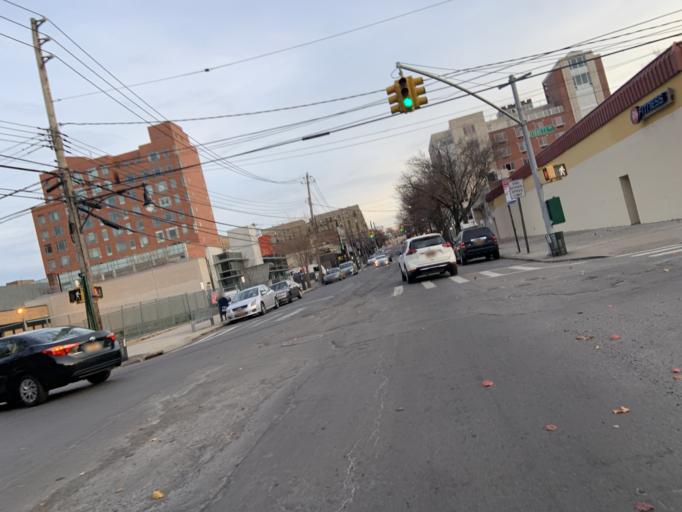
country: US
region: New York
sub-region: New York County
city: Inwood
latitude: 40.8809
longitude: -73.9085
